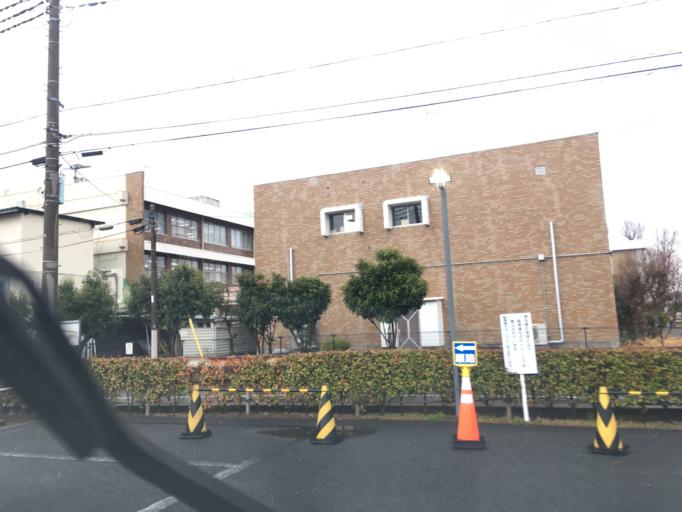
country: JP
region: Saitama
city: Koshigaya
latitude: 35.8920
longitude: 139.7902
